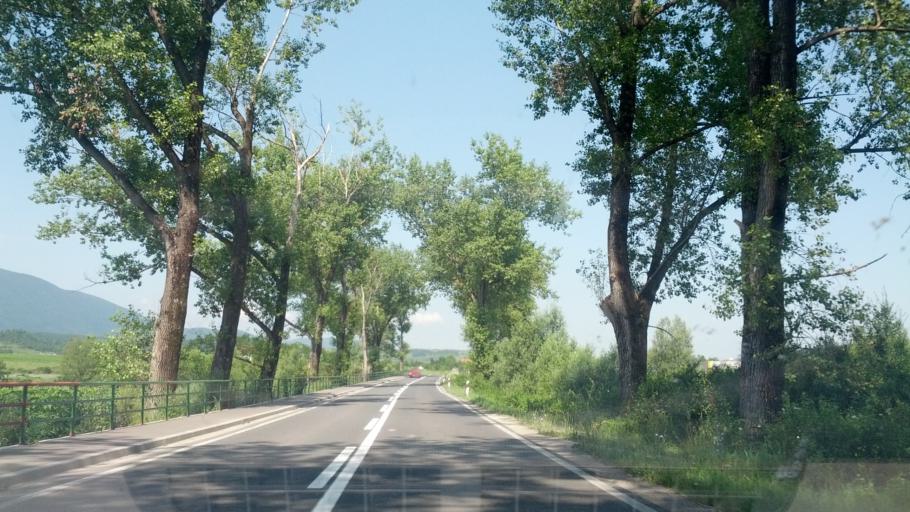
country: BA
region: Federation of Bosnia and Herzegovina
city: Bihac
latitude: 44.8279
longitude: 15.8389
